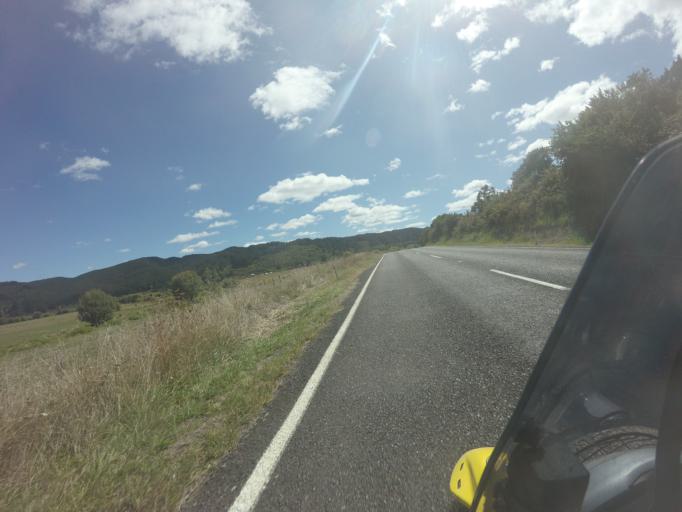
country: NZ
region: Bay of Plenty
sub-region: Kawerau District
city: Kawerau
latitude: -38.1887
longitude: 176.8389
